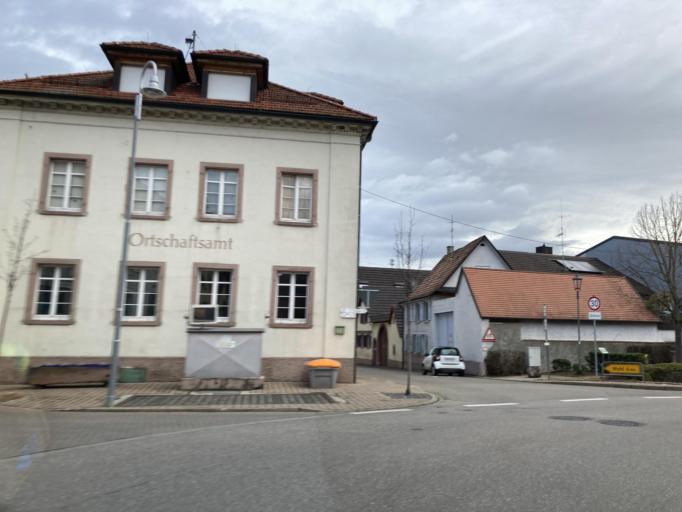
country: DE
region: Baden-Wuerttemberg
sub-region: Freiburg Region
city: Wyhl
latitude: 48.1336
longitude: 7.6548
